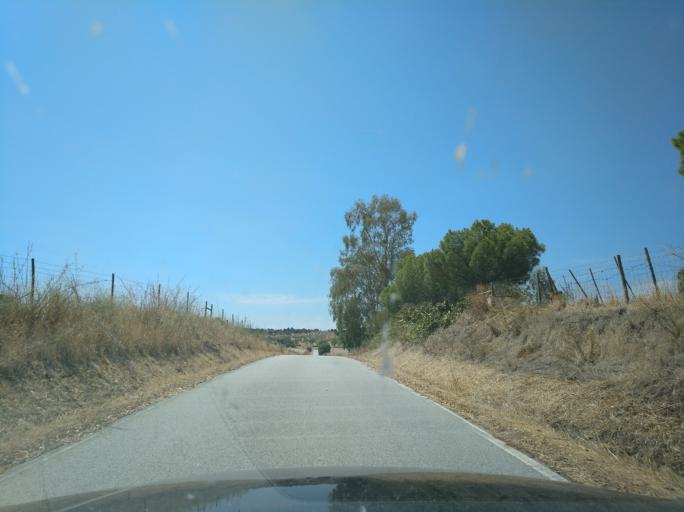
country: PT
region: Portalegre
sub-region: Campo Maior
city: Campo Maior
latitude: 38.9622
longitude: -7.1148
